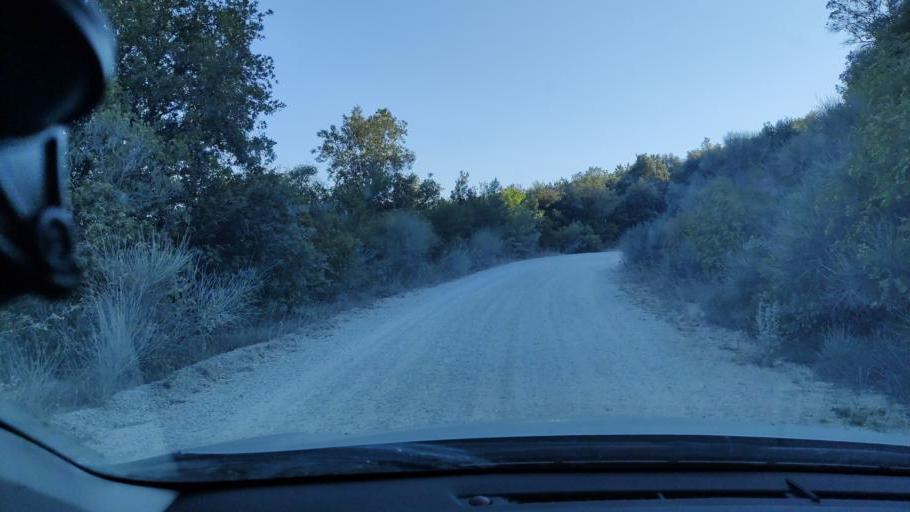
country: IT
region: Umbria
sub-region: Provincia di Terni
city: Amelia
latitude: 42.5364
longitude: 12.3815
